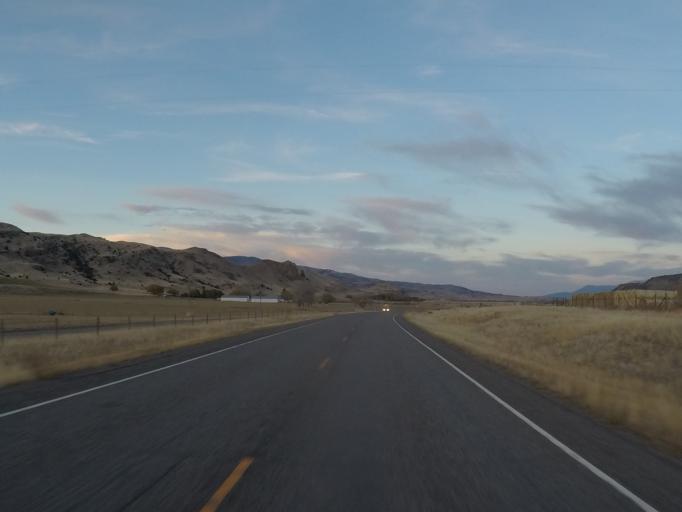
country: US
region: Montana
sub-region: Gallatin County
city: Bozeman
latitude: 45.2722
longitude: -110.8595
